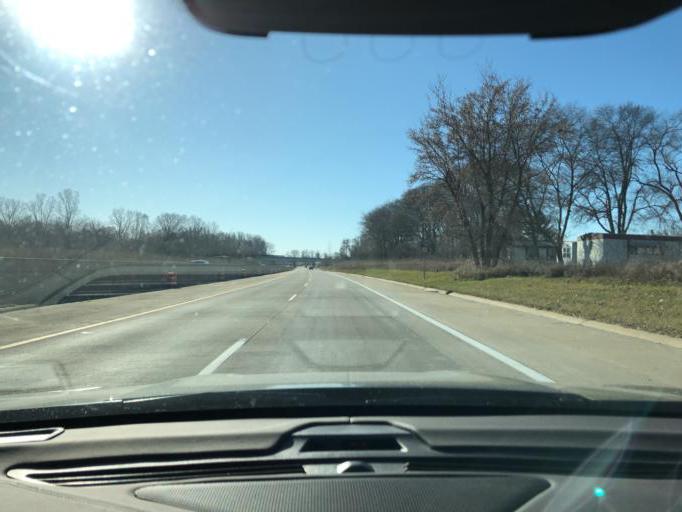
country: US
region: Michigan
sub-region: Wayne County
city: Belleville
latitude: 42.2551
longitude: -83.5383
